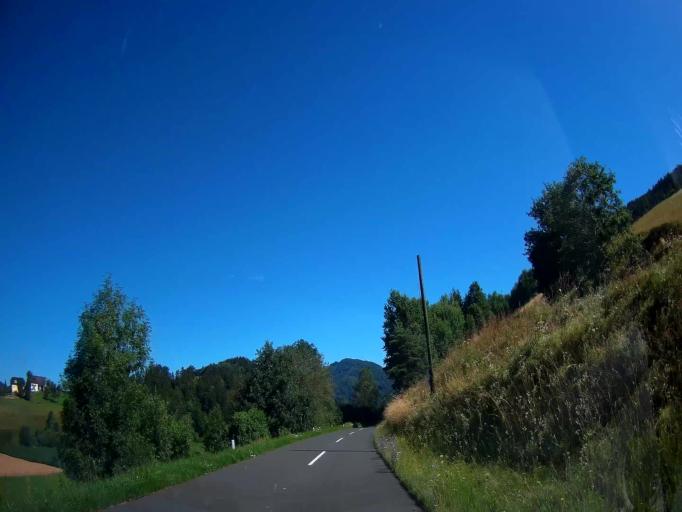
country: AT
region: Carinthia
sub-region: Politischer Bezirk Volkermarkt
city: Voelkermarkt
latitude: 46.6816
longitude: 14.5766
